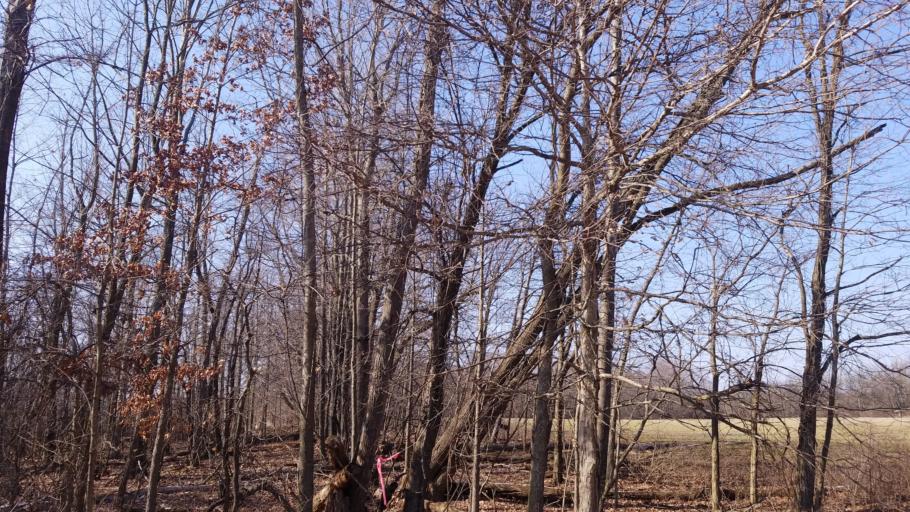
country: US
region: Ohio
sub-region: Richland County
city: Lincoln Heights
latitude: 40.8216
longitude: -82.5229
